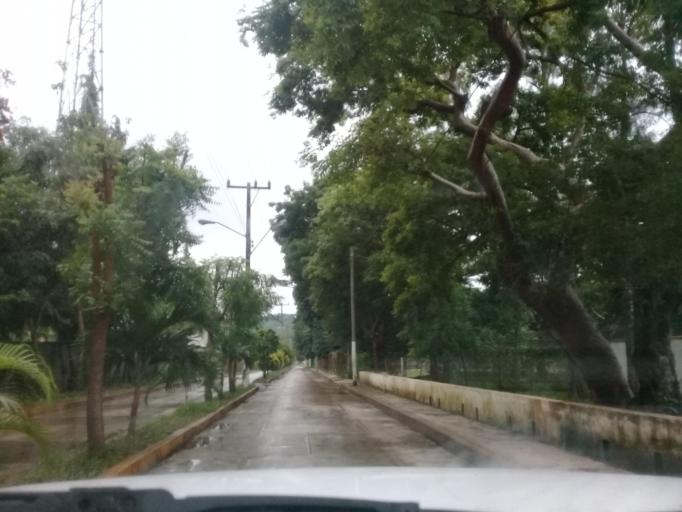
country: MX
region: Veracruz
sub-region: San Andres Tuxtla
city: Cerro las Iguanas
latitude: 18.4250
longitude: -95.2195
